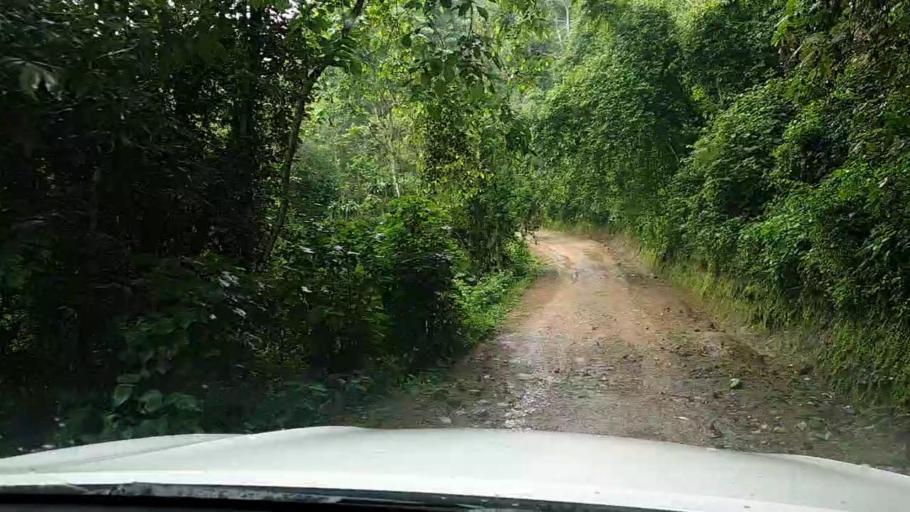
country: RW
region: Western Province
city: Cyangugu
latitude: -2.5588
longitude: 28.9848
